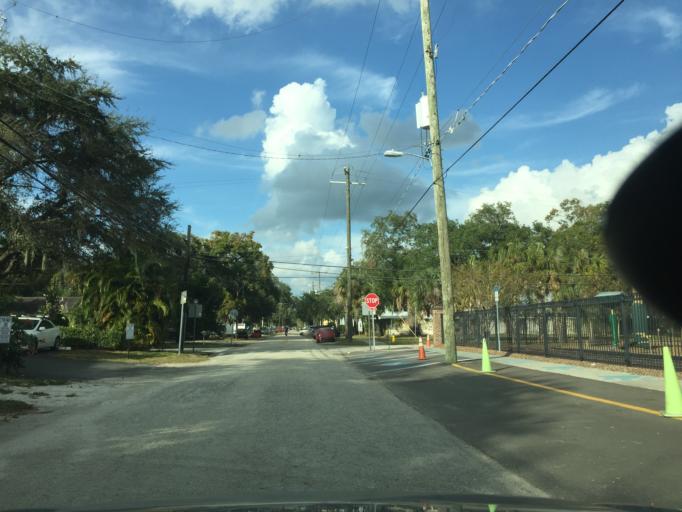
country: US
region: Florida
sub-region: Hillsborough County
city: Tampa
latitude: 27.9431
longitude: -82.4913
